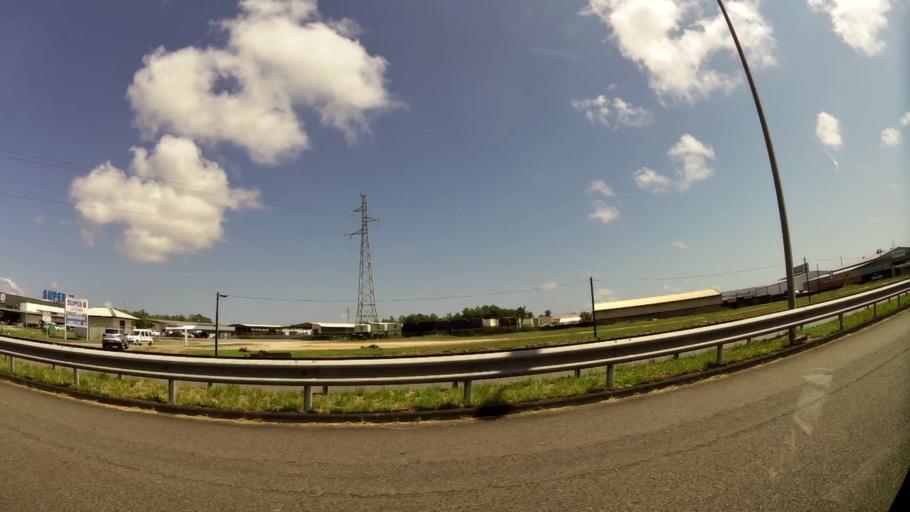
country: GF
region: Guyane
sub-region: Guyane
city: Cayenne
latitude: 4.9235
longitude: -52.3255
